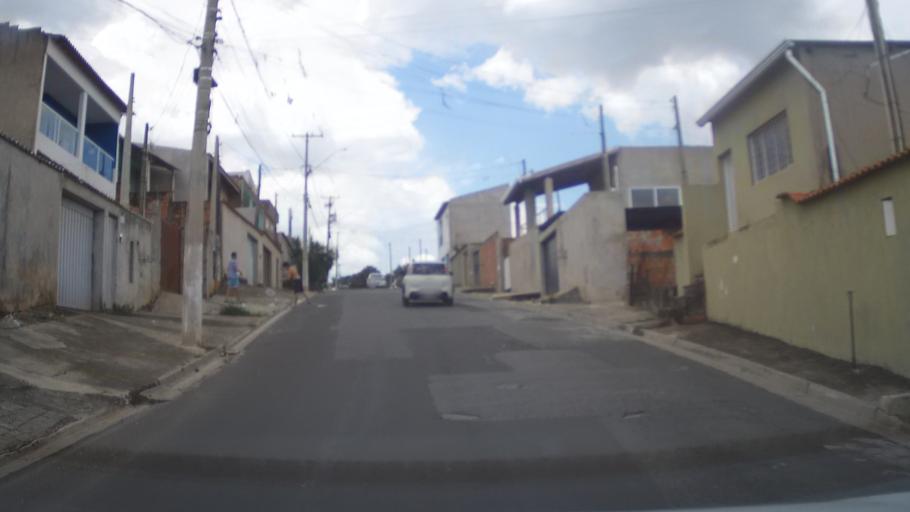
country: BR
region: Sao Paulo
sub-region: Campinas
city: Campinas
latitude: -22.9188
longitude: -47.0231
